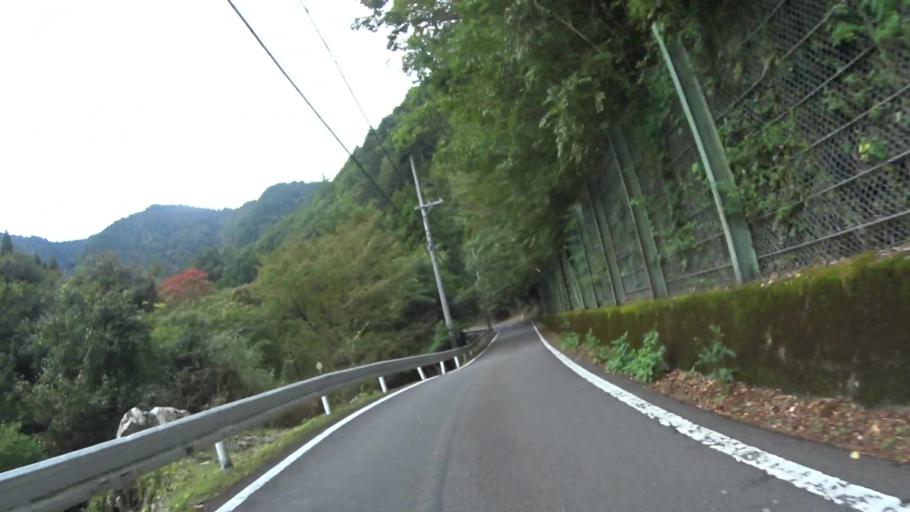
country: JP
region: Fukui
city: Obama
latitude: 35.3124
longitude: 135.6918
